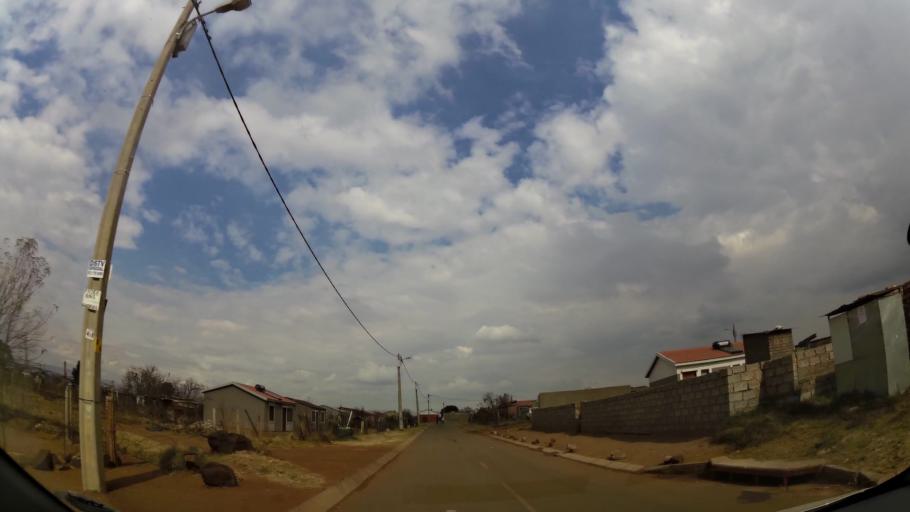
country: ZA
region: Gauteng
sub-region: Ekurhuleni Metropolitan Municipality
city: Germiston
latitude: -26.3904
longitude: 28.1545
